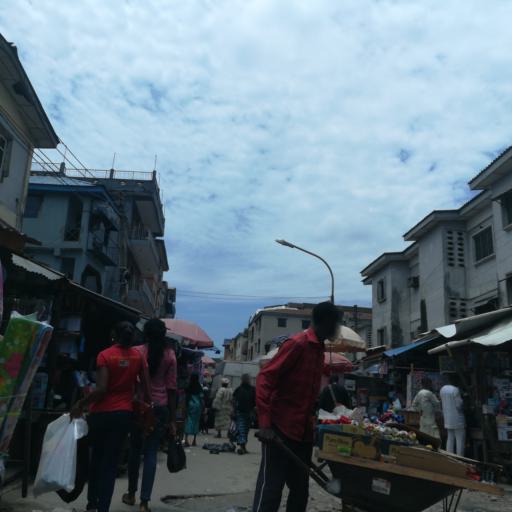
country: NG
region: Lagos
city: Lagos
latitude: 6.4608
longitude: 3.3894
